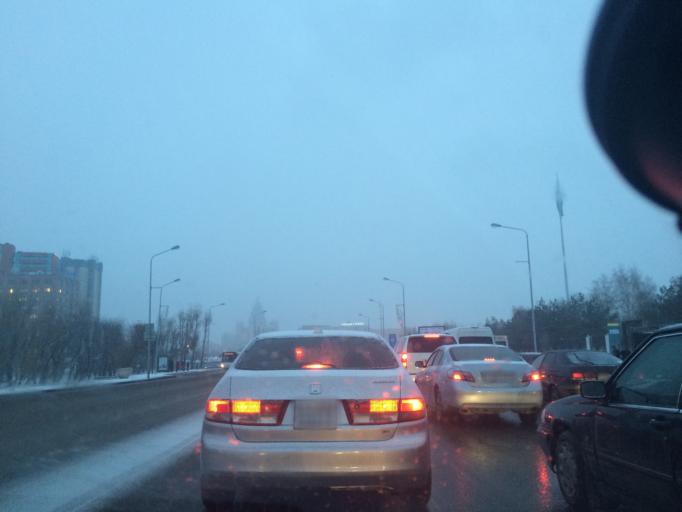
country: KZ
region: Astana Qalasy
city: Astana
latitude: 51.1500
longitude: 71.4254
